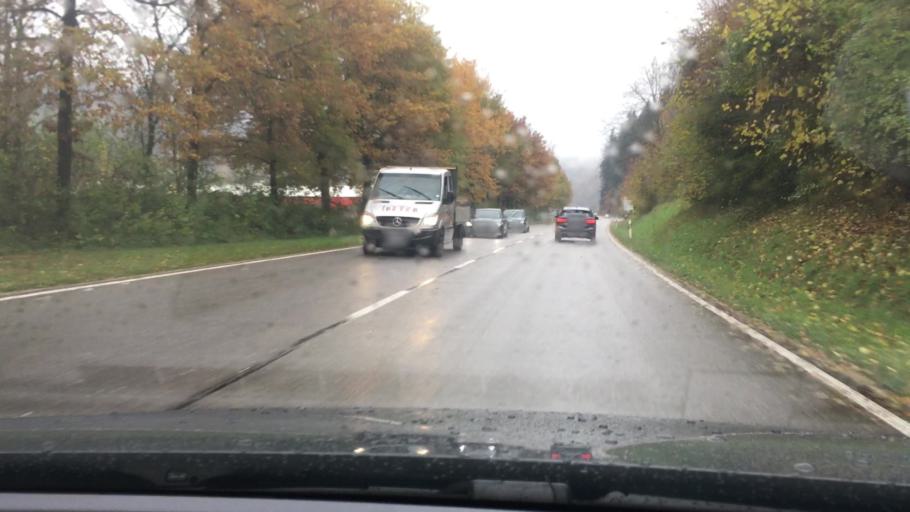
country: DE
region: Baden-Wuerttemberg
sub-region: Freiburg Region
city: Oppenau
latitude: 48.4766
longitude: 8.1547
